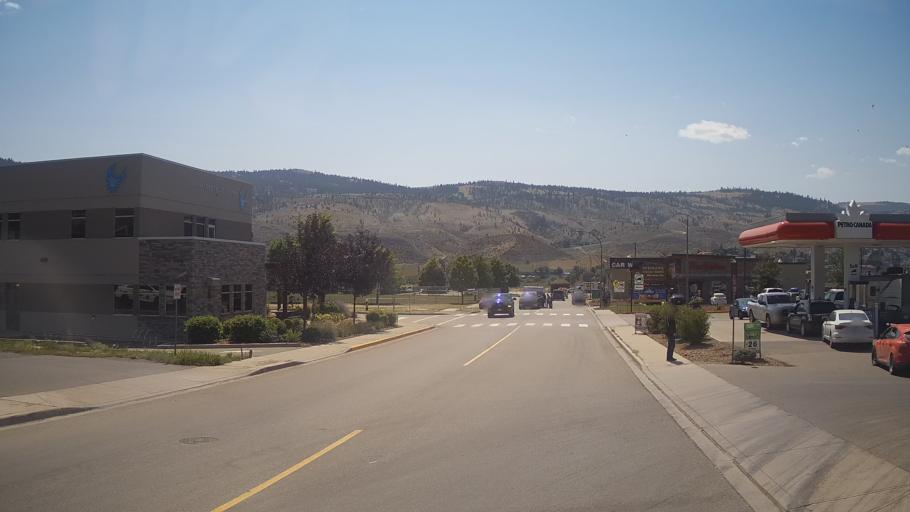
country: CA
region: British Columbia
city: Kamloops
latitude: 50.6817
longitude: -120.2971
